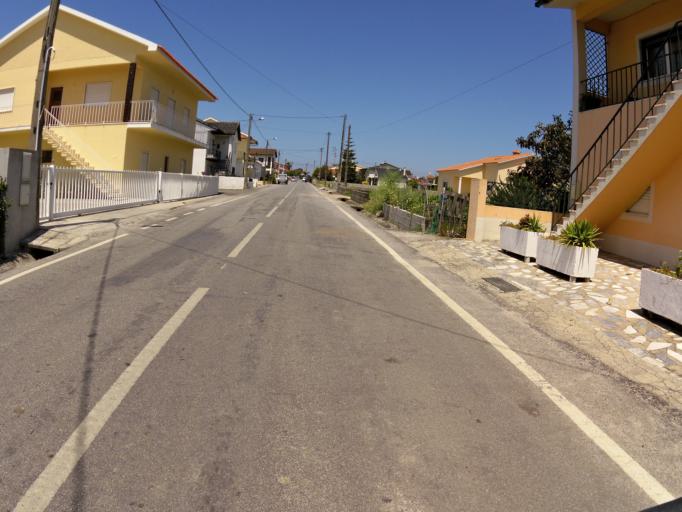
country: PT
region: Coimbra
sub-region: Montemor-O-Velho
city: Montemor-o-Velho
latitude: 40.1538
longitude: -8.7106
